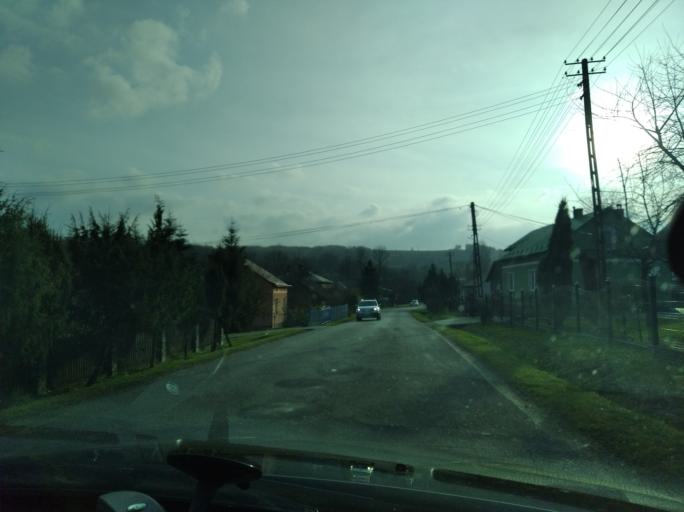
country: PL
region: Subcarpathian Voivodeship
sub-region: Powiat przeworski
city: Lopuszka Wielka
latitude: 49.9415
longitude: 22.4023
